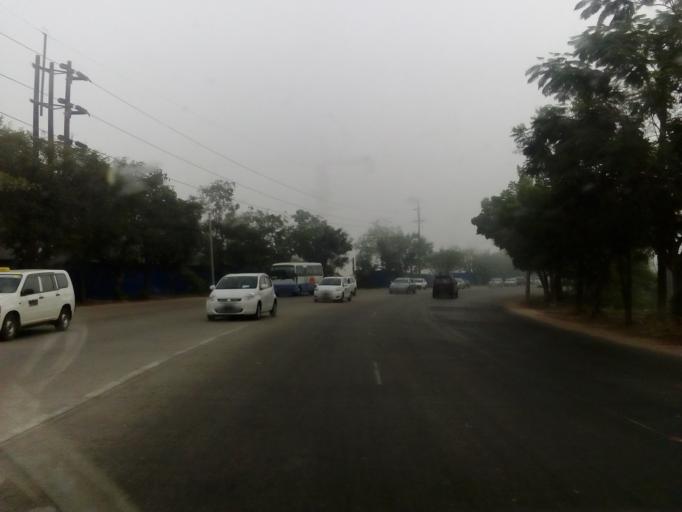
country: MM
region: Yangon
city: Yangon
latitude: 16.8124
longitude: 96.1854
